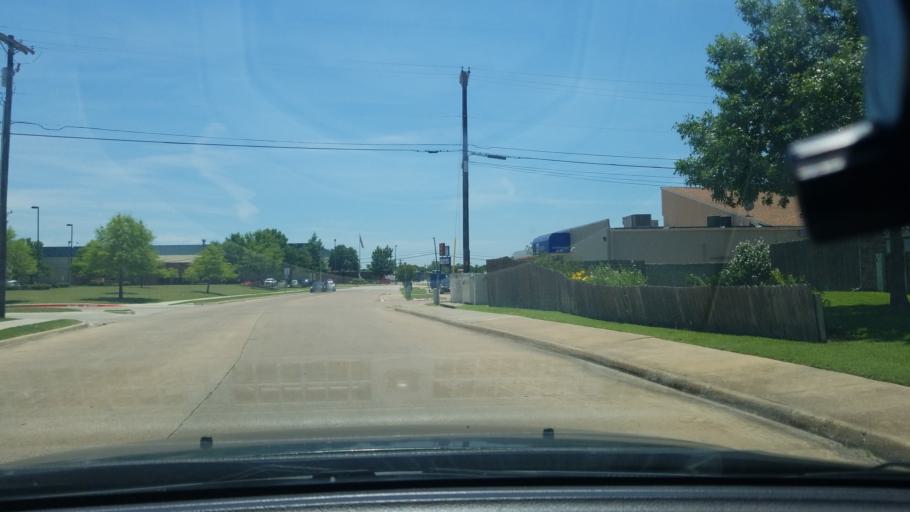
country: US
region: Texas
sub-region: Dallas County
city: Mesquite
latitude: 32.7721
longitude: -96.6081
